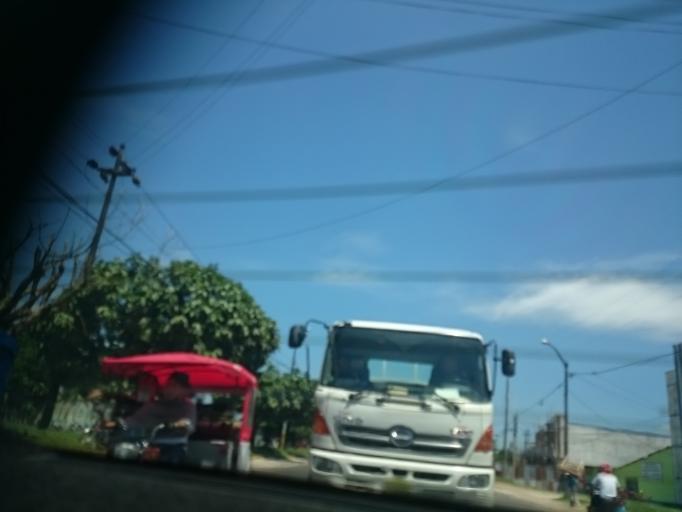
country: PE
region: Loreto
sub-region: Provincia de Maynas
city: Iquitos
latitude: -3.7798
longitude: -73.2939
